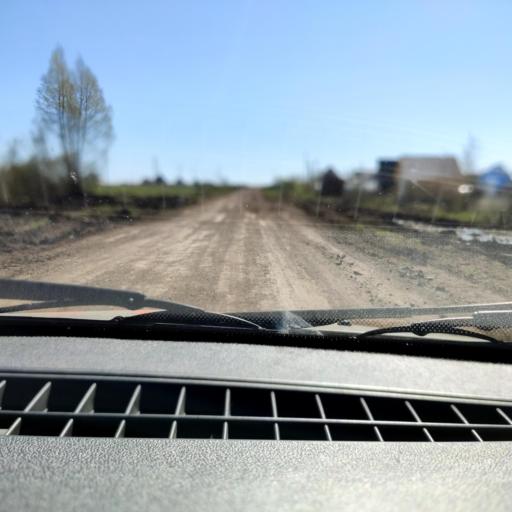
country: RU
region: Bashkortostan
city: Iglino
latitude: 54.8143
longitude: 56.4359
